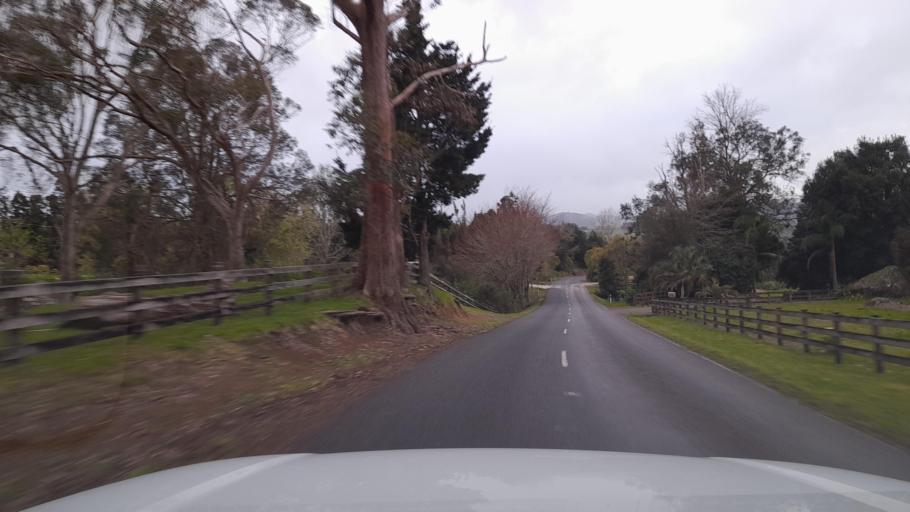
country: NZ
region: Northland
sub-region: Whangarei
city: Maungatapere
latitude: -35.6386
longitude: 174.2071
